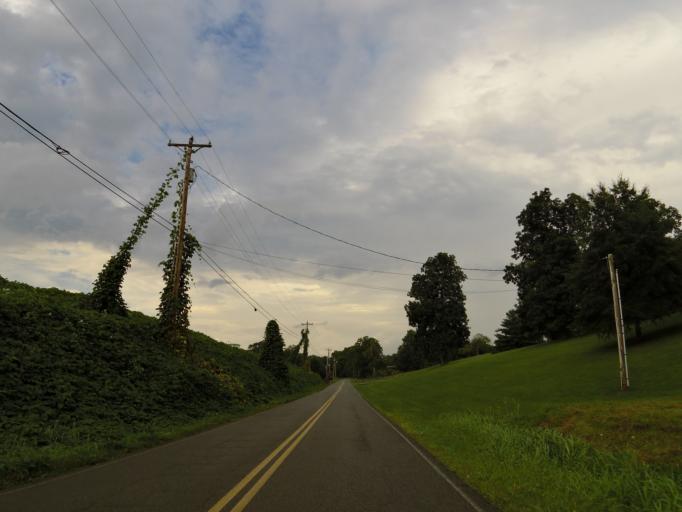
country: US
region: Tennessee
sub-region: Blount County
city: Wildwood
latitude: 35.8269
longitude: -83.8498
